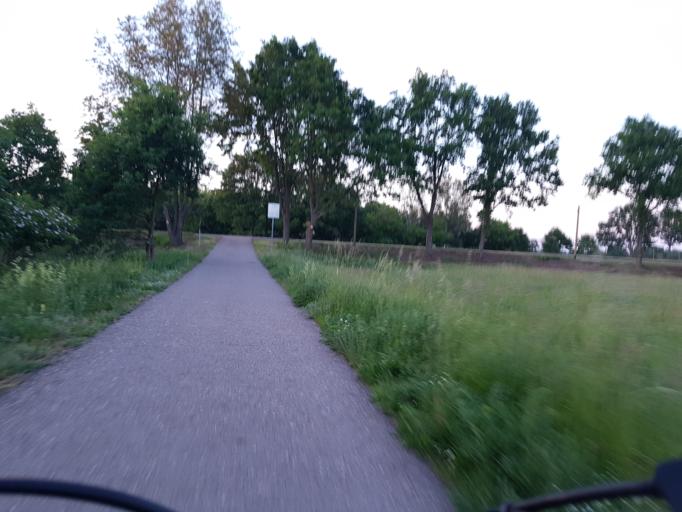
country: DE
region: Brandenburg
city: Falkenberg
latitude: 51.6087
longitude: 13.3057
